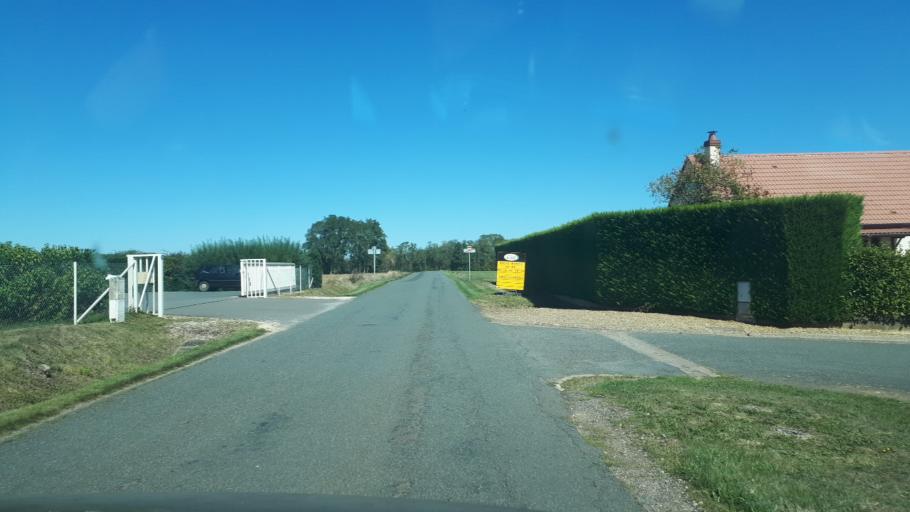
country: FR
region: Centre
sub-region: Departement du Cher
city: Rians
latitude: 47.1877
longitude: 2.7127
